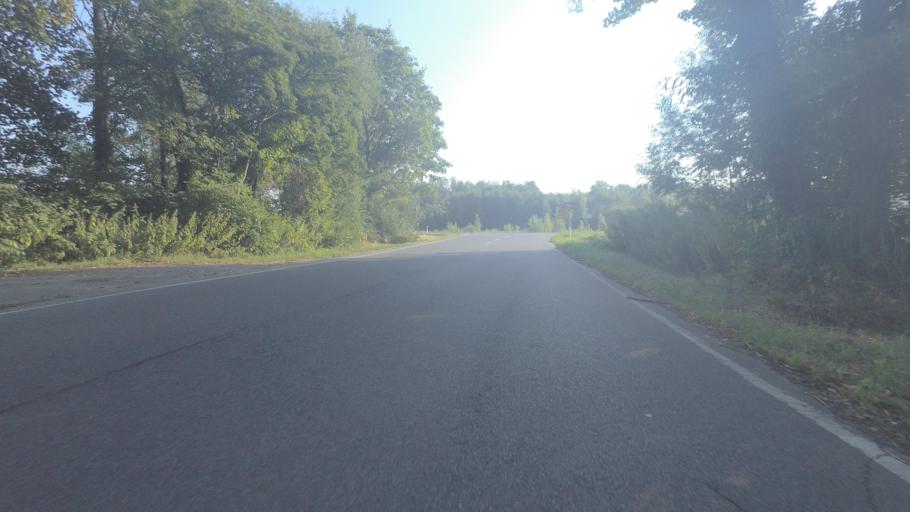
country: DE
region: Mecklenburg-Vorpommern
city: Demmin
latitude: 53.9602
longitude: 13.1316
